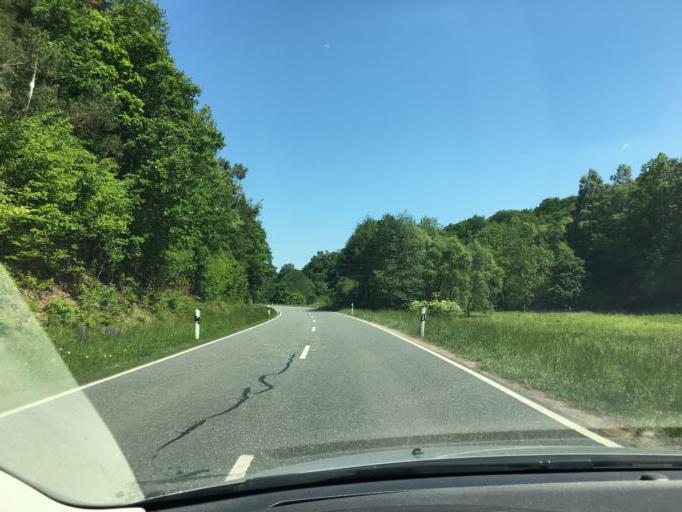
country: DE
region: Hesse
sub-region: Regierungsbezirk Kassel
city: Ronshausen
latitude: 50.9423
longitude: 9.8947
